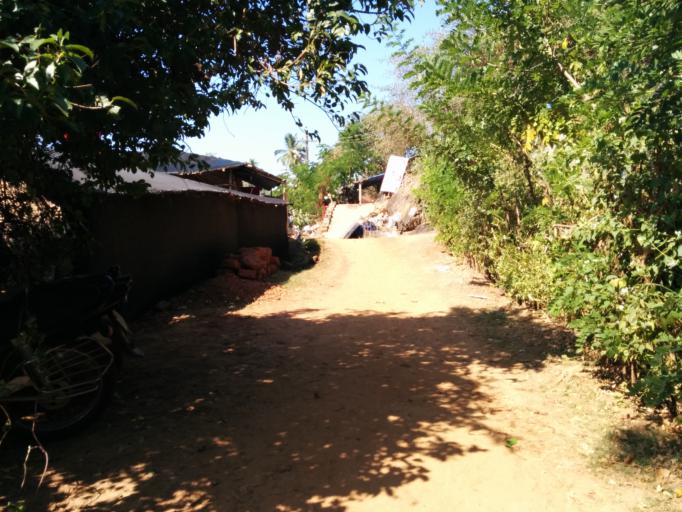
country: IN
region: Karnataka
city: Canacona
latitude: 14.9999
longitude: 74.0308
